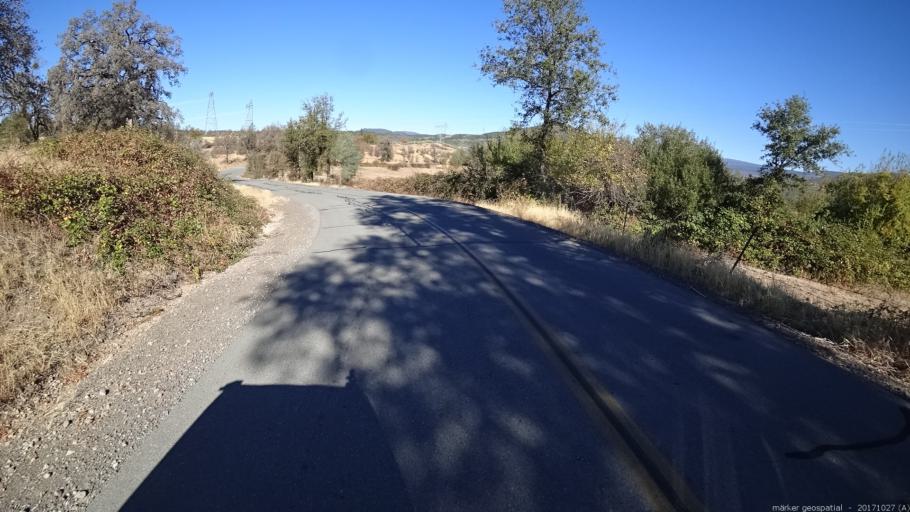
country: US
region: California
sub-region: Shasta County
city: Shingletown
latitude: 40.7671
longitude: -121.9696
